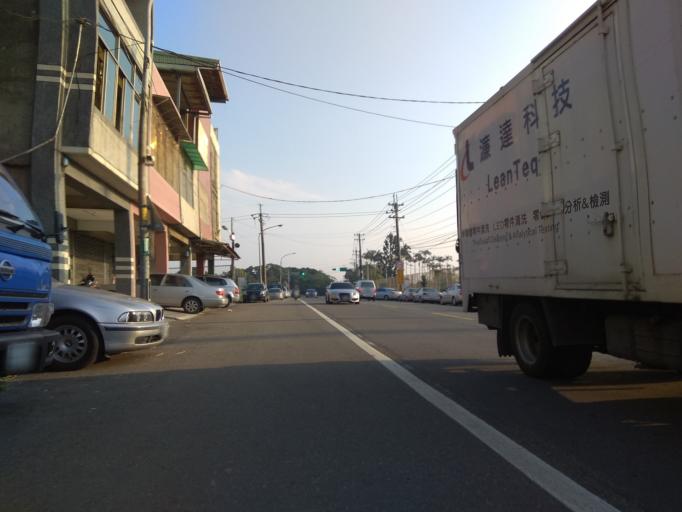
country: TW
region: Taiwan
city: Daxi
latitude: 24.9129
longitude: 121.1876
